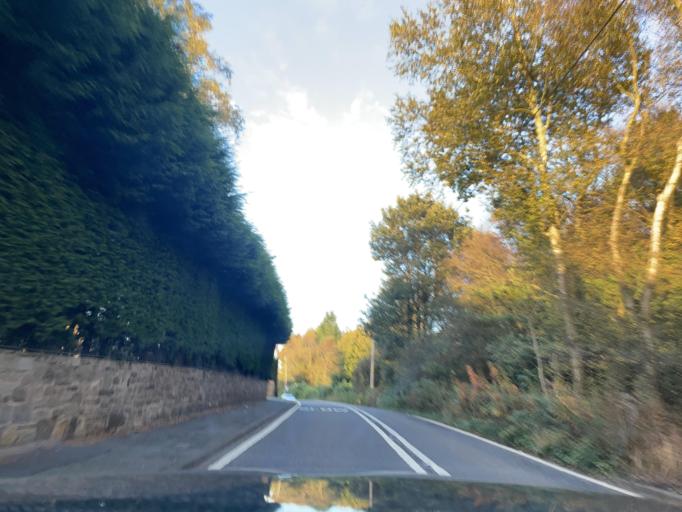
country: GB
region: England
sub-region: Borough of Stockport
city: Marple
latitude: 53.4220
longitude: -2.0292
